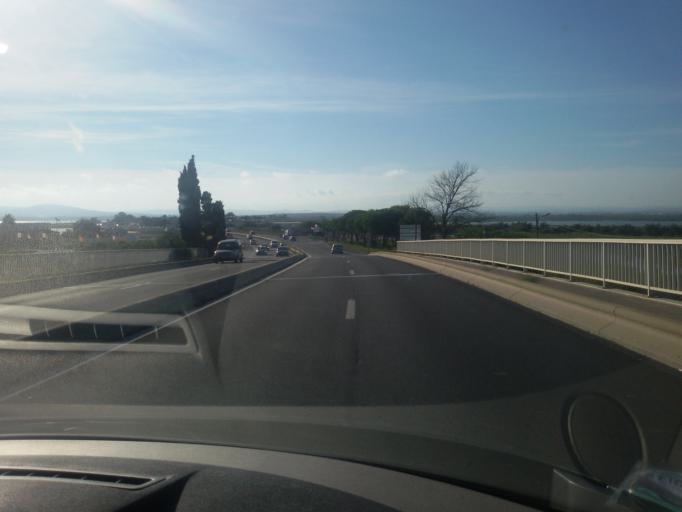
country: FR
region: Languedoc-Roussillon
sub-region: Departement de l'Herault
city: Palavas-les-Flots
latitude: 43.5341
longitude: 3.9162
